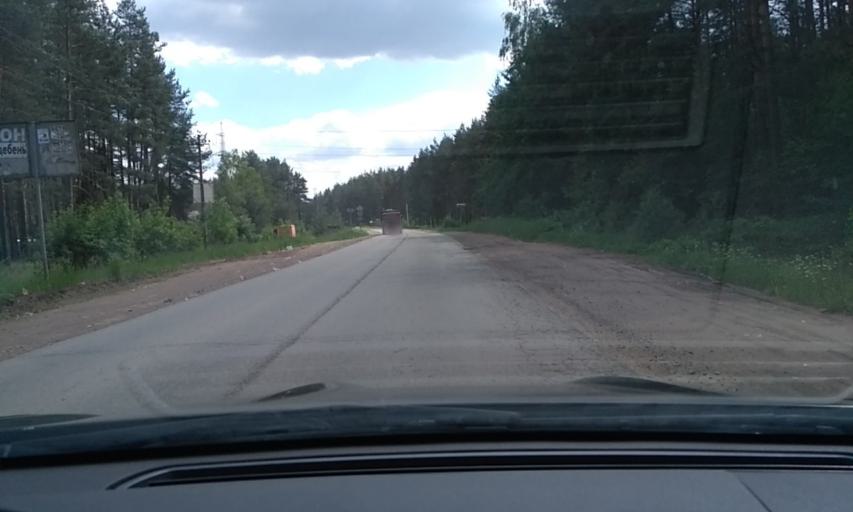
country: RU
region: Leningrad
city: Imeni Sverdlova
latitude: 59.8574
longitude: 30.6726
